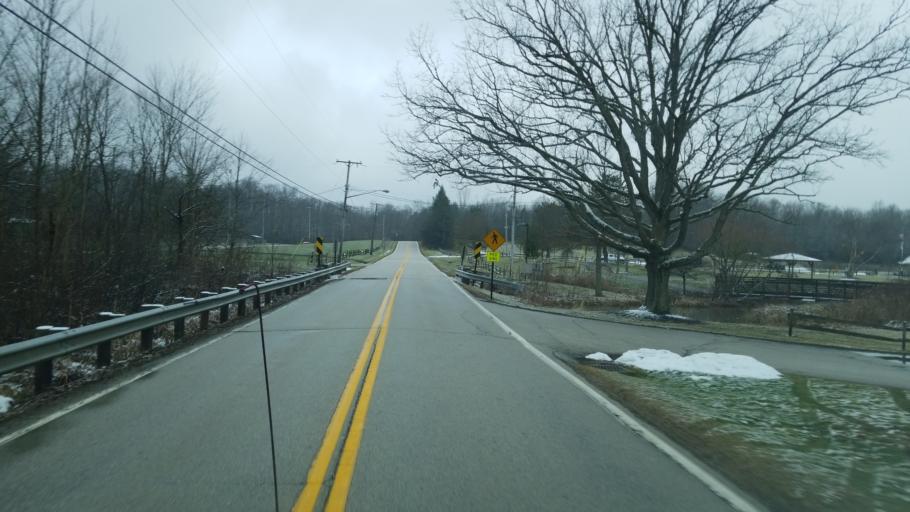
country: US
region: Ohio
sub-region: Portage County
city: Aurora
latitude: 41.2900
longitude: -81.3173
